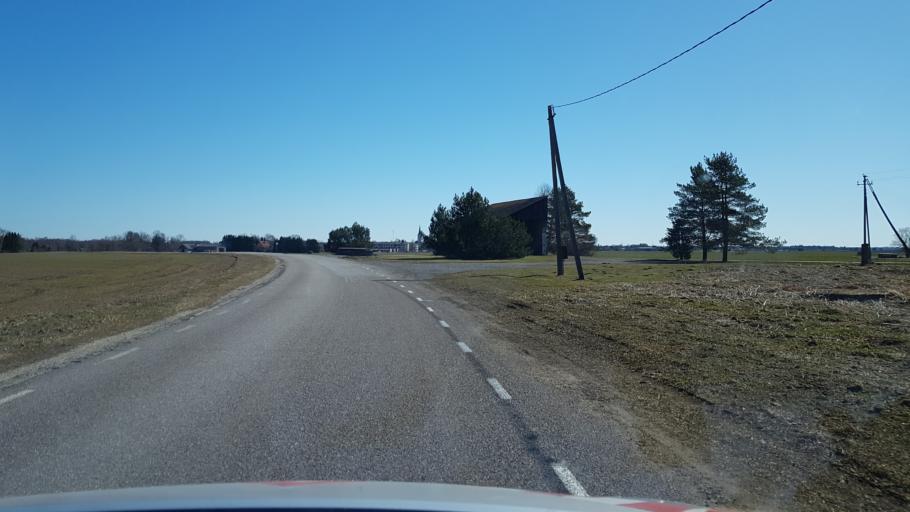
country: EE
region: Laeaene-Virumaa
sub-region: Haljala vald
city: Haljala
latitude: 59.4329
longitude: 26.2424
